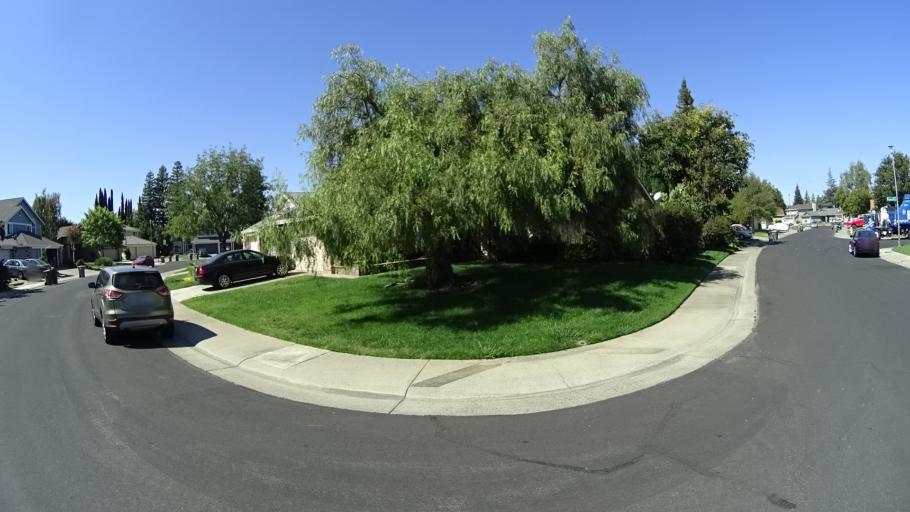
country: US
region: California
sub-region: Sacramento County
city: Laguna
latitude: 38.4257
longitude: -121.4321
